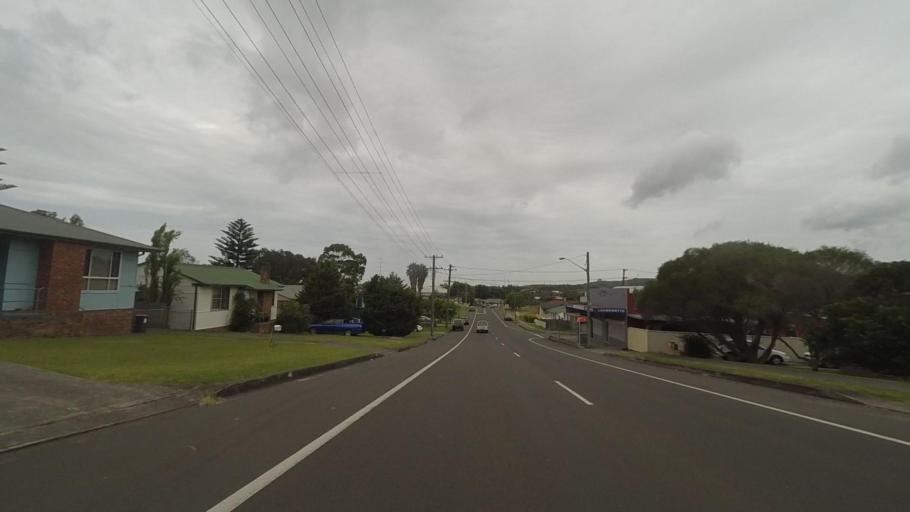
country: AU
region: New South Wales
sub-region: Wollongong
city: Cordeaux Heights
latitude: -34.4583
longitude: 150.8334
